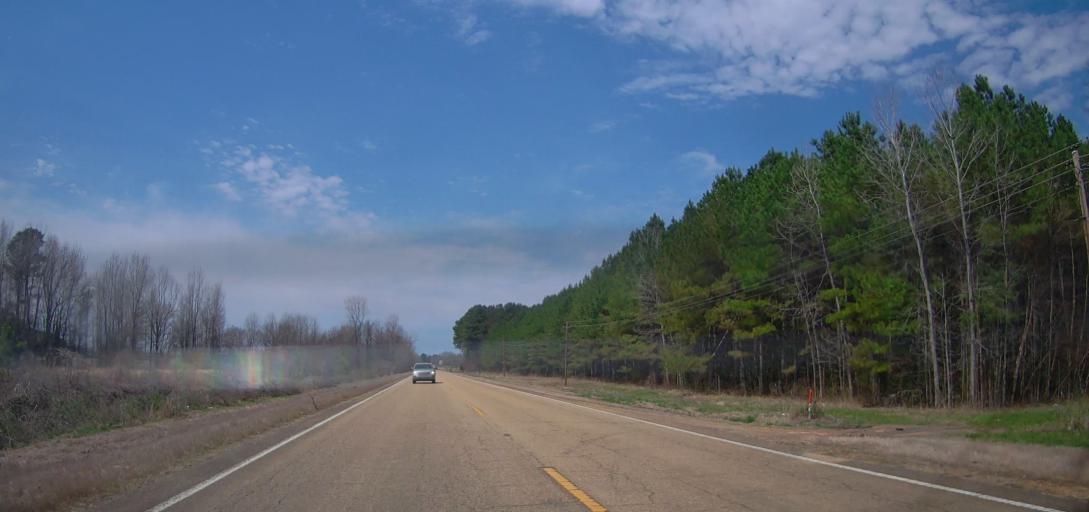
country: US
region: Mississippi
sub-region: Union County
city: New Albany
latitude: 34.6146
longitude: -89.1579
